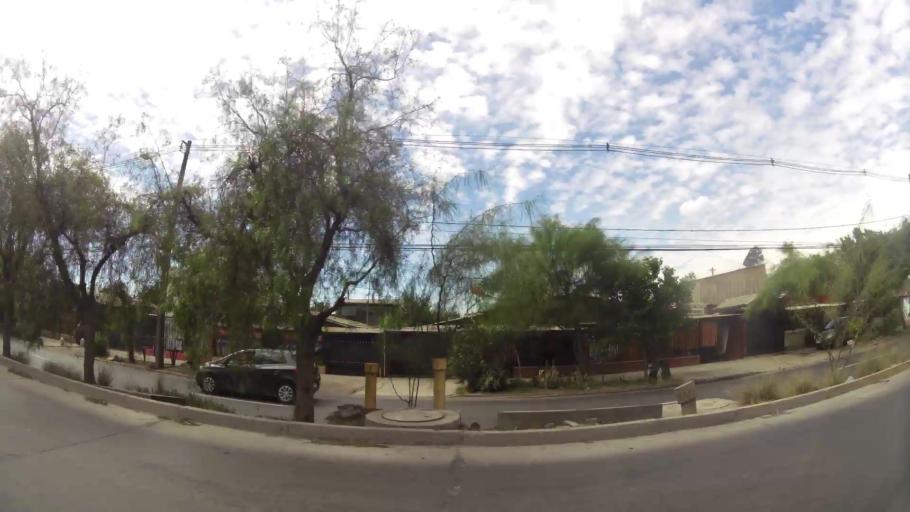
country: CL
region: Santiago Metropolitan
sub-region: Provincia de Santiago
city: La Pintana
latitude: -33.5855
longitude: -70.6611
